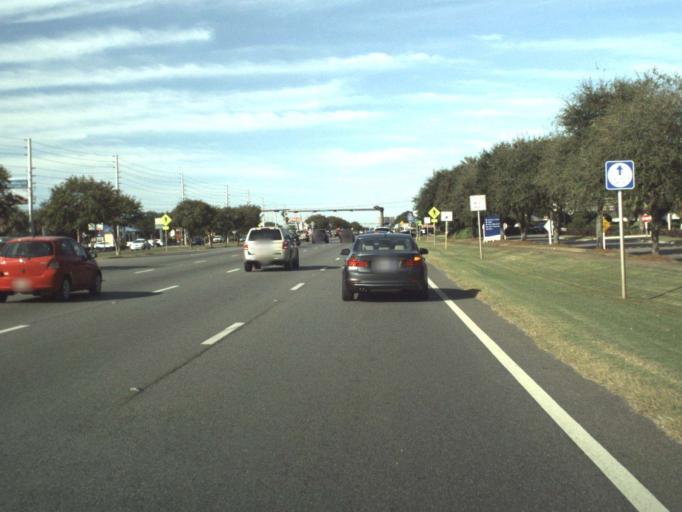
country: US
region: Florida
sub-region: Walton County
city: Miramar Beach
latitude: 30.3894
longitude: -86.4242
